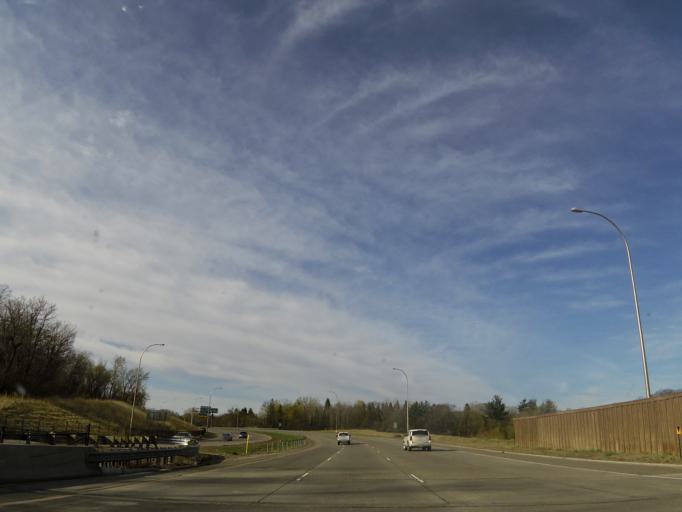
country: US
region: Minnesota
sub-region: Hennepin County
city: Edina
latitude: 44.8525
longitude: -93.3967
